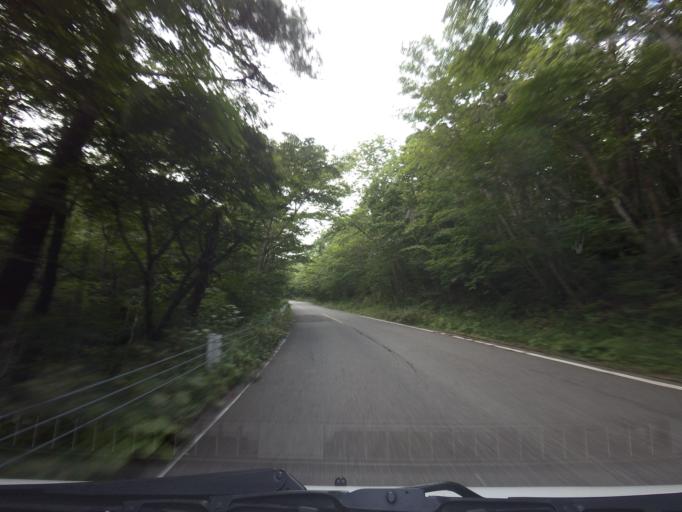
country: JP
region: Fukushima
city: Nihommatsu
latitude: 37.6161
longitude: 140.3397
